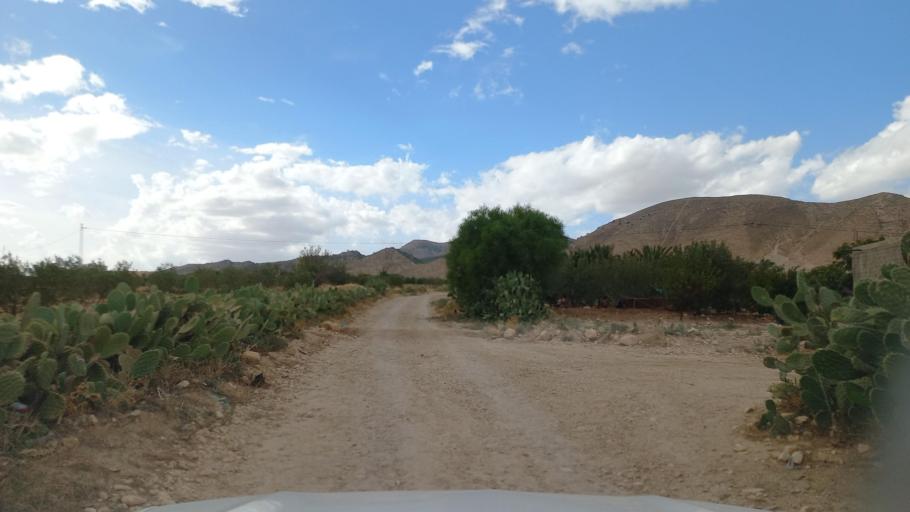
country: TN
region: Al Qasrayn
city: Sbiba
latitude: 35.4493
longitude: 9.0714
